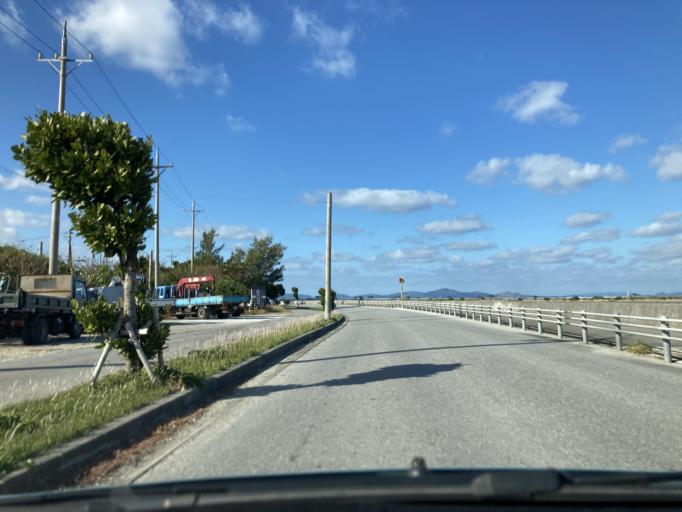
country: JP
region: Okinawa
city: Katsuren-haebaru
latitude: 26.3249
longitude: 127.9127
